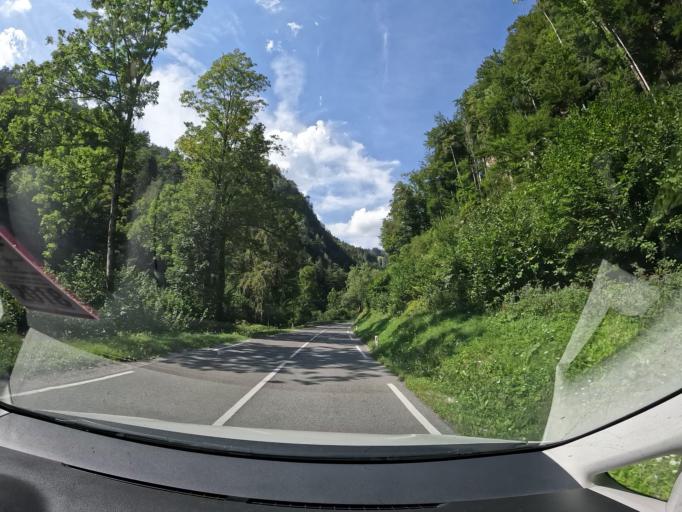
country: SI
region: Trzic
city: Trzic
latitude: 46.3952
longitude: 14.3441
